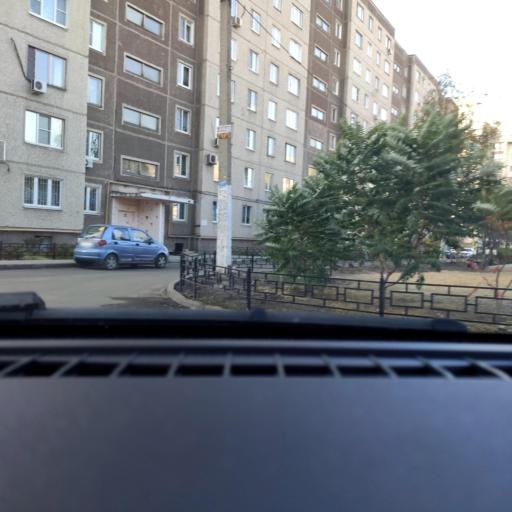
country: RU
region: Voronezj
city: Voronezh
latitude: 51.6714
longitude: 39.2456
